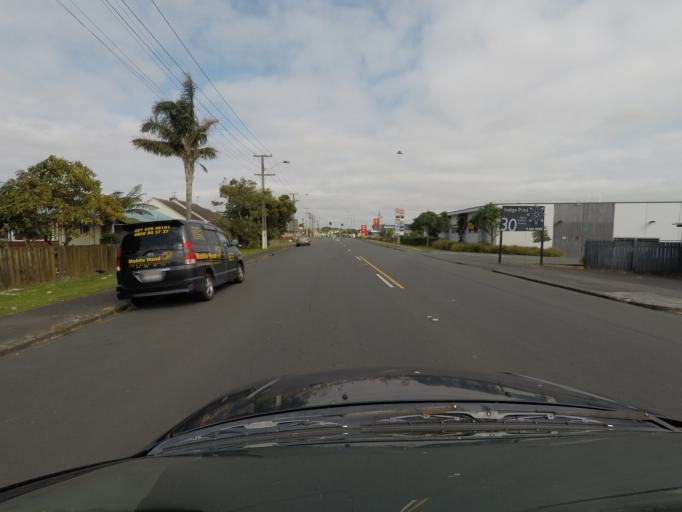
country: NZ
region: Auckland
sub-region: Auckland
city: Auckland
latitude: -36.9068
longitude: 174.7330
